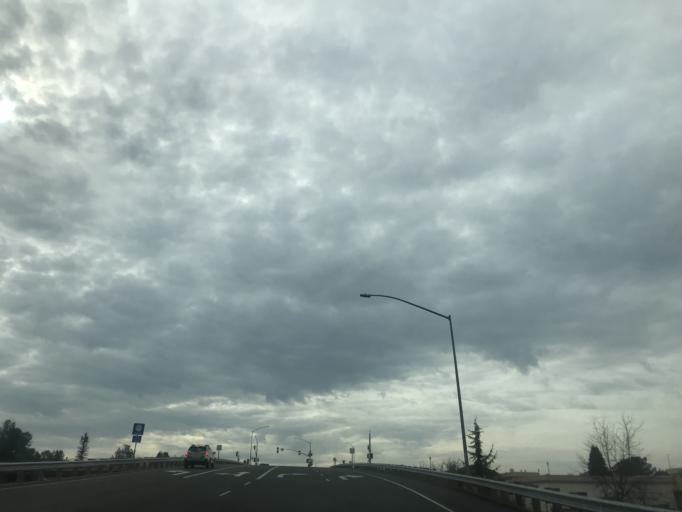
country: US
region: California
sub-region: El Dorado County
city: Diamond Springs
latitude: 38.7131
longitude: -120.8388
